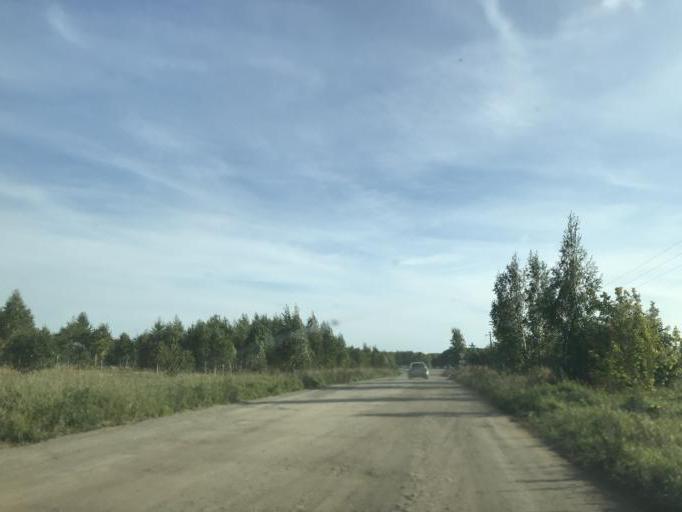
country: RU
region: Chelyabinsk
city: Poletayevo
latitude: 54.9742
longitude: 60.9705
